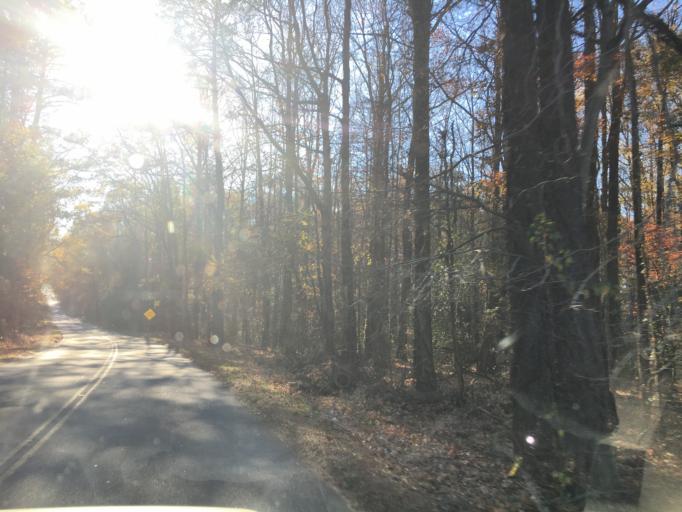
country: US
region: South Carolina
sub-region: Spartanburg County
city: Wellford
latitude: 34.9359
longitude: -82.0751
